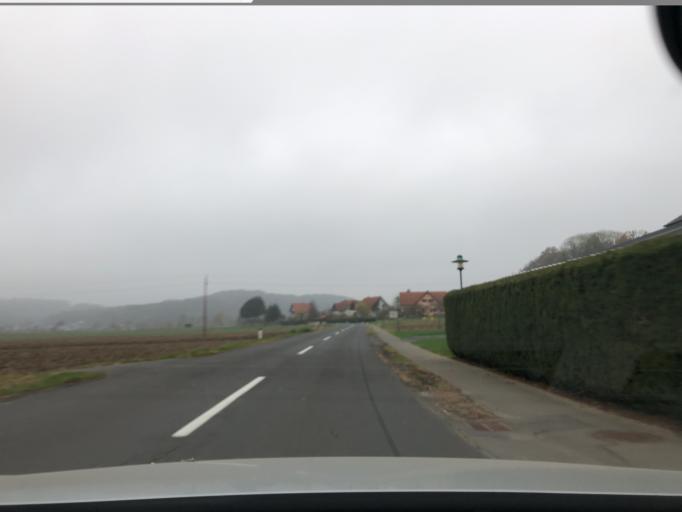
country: AT
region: Styria
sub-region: Politischer Bezirk Suedoststeiermark
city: Fehring
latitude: 46.9568
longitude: 16.0285
